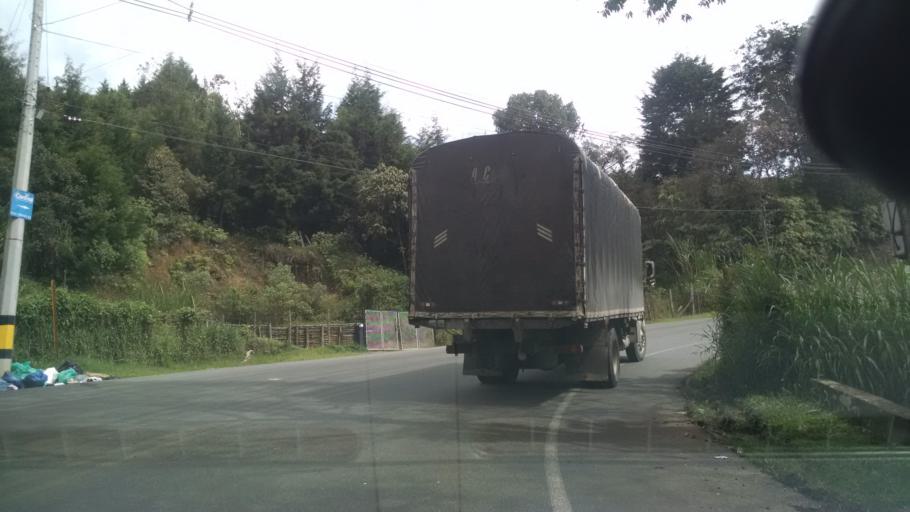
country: CO
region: Antioquia
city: Caldas
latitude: 6.0325
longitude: -75.6235
